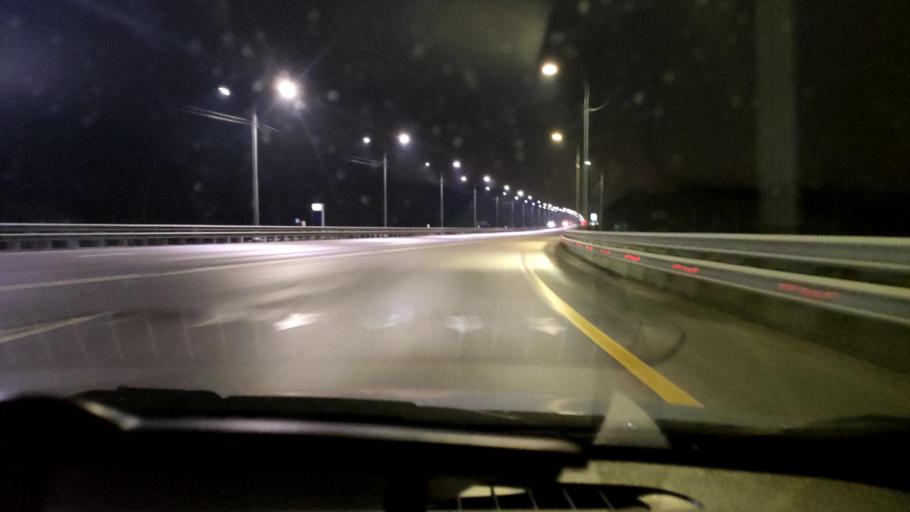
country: RU
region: Voronezj
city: Ramon'
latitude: 51.8876
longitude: 39.2173
